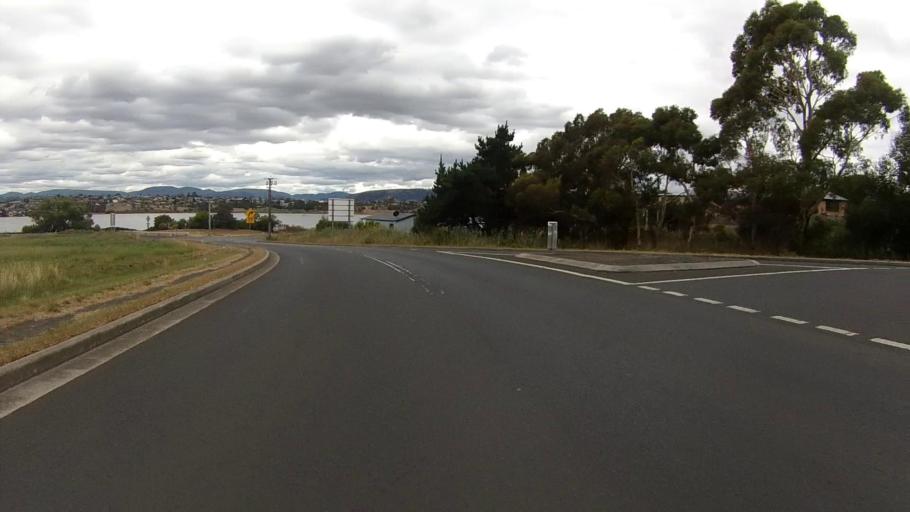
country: AU
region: Tasmania
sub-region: Glenorchy
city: Granton
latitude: -42.7522
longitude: 147.2289
